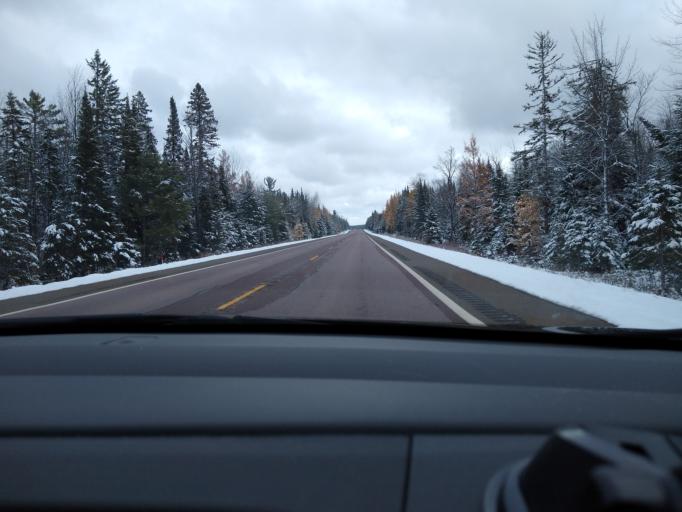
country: US
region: Michigan
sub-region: Iron County
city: Iron River
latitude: 46.1667
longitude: -88.9153
